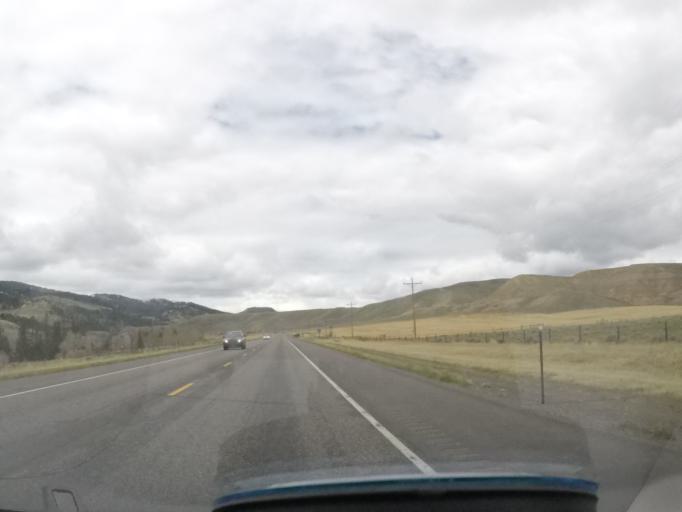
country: US
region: Wyoming
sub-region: Sublette County
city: Pinedale
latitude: 43.5764
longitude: -109.7359
